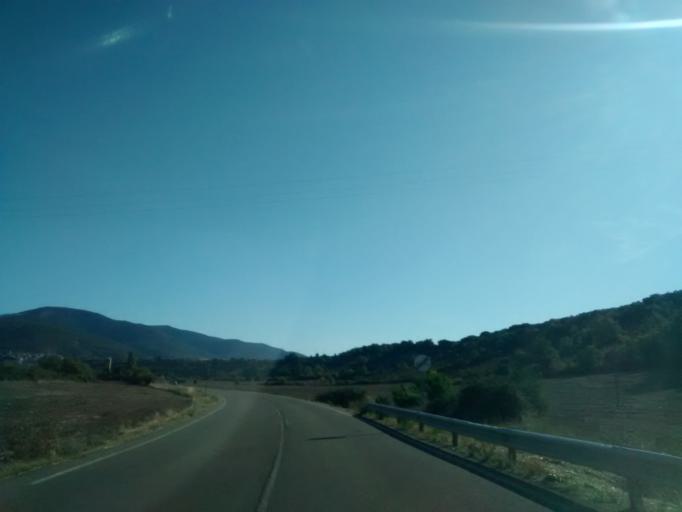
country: ES
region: Aragon
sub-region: Provincia de Huesca
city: Bailo
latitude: 42.5760
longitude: -0.7548
